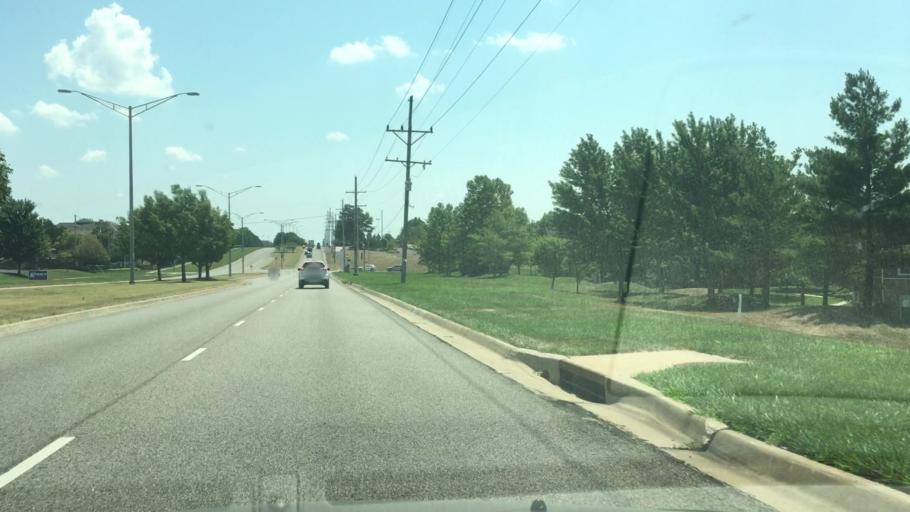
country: US
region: Kansas
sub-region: Johnson County
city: Lenexa
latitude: 38.8836
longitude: -94.7188
